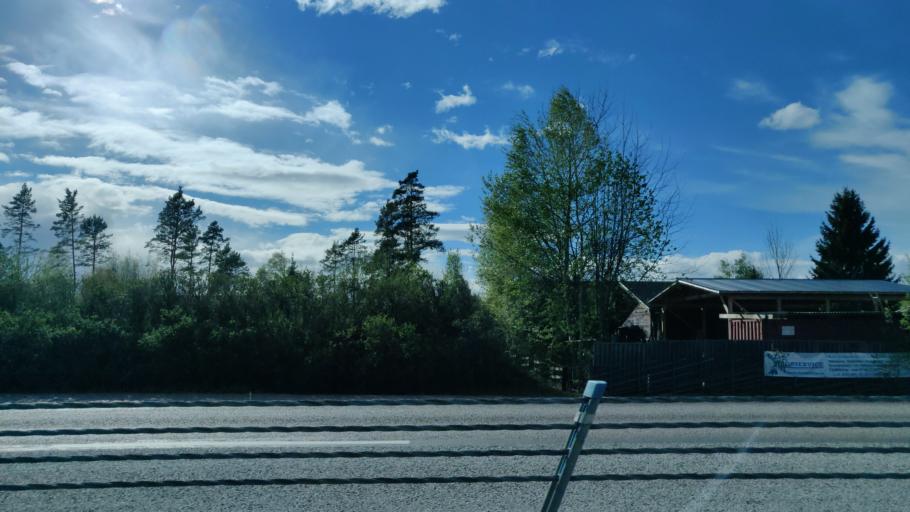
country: SE
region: Vaermland
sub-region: Forshaga Kommun
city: Forshaga
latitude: 59.4781
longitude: 13.4108
